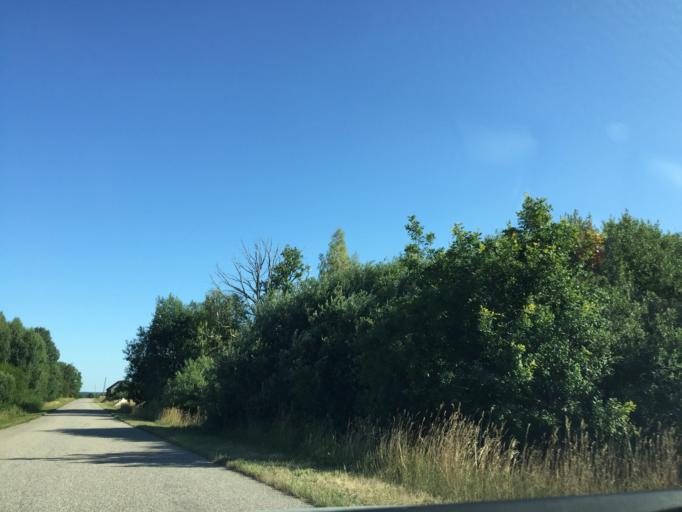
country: LV
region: Talsu Rajons
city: Stende
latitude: 57.1516
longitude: 22.6234
